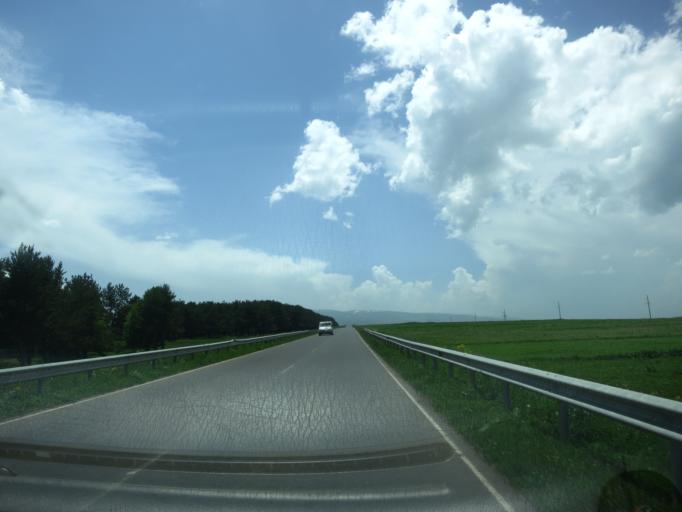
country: GE
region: Samtskhe-Javakheti
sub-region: Ninotsminda
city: Ninotsminda
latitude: 41.2844
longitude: 43.6296
